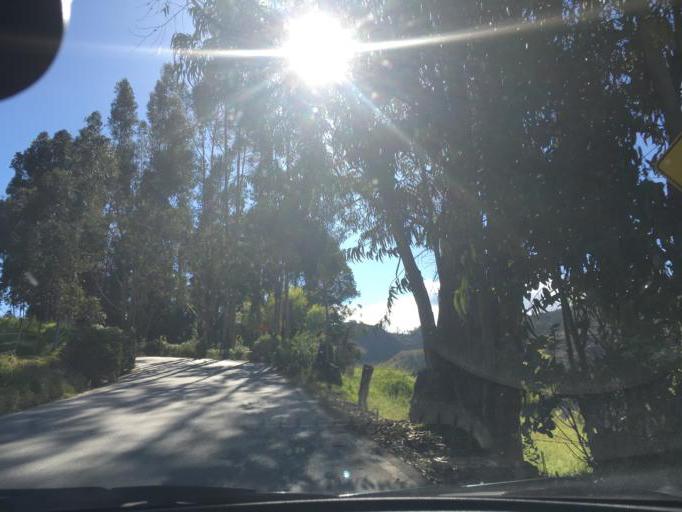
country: CO
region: Boyaca
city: Firavitoba
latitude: 5.5948
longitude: -72.9790
